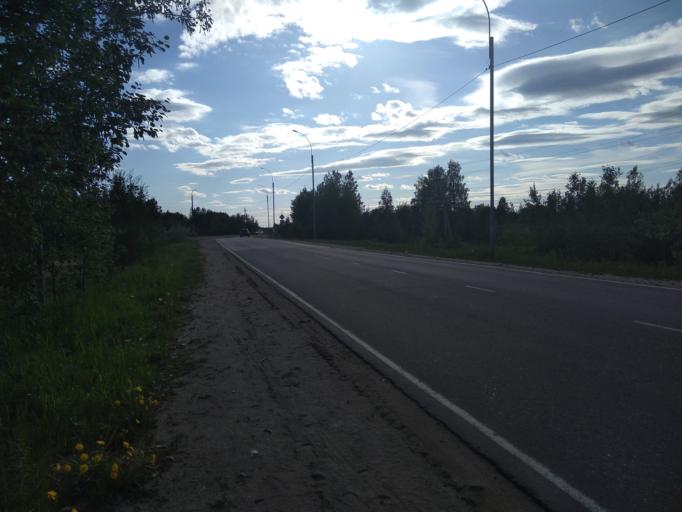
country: RU
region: Komi Republic
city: Puteyets
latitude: 65.1360
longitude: 57.1443
